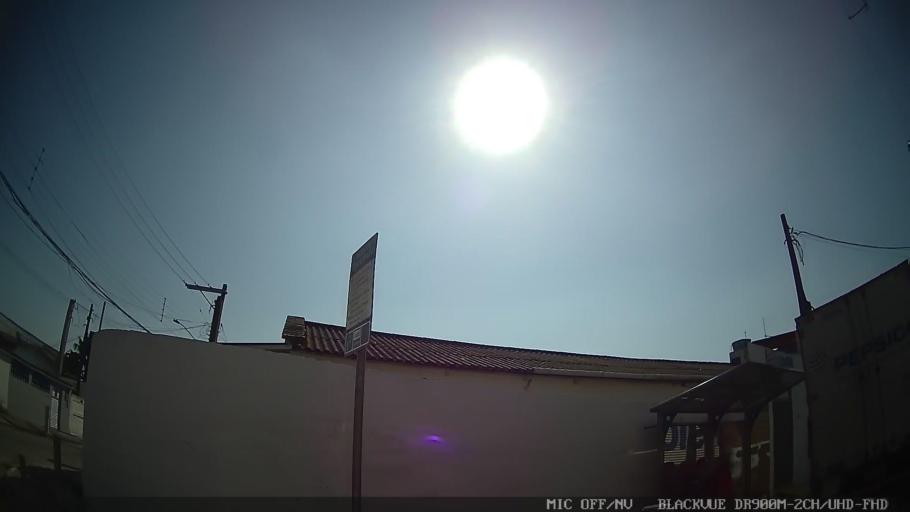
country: BR
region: Sao Paulo
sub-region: Santos
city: Santos
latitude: -23.9969
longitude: -46.3044
